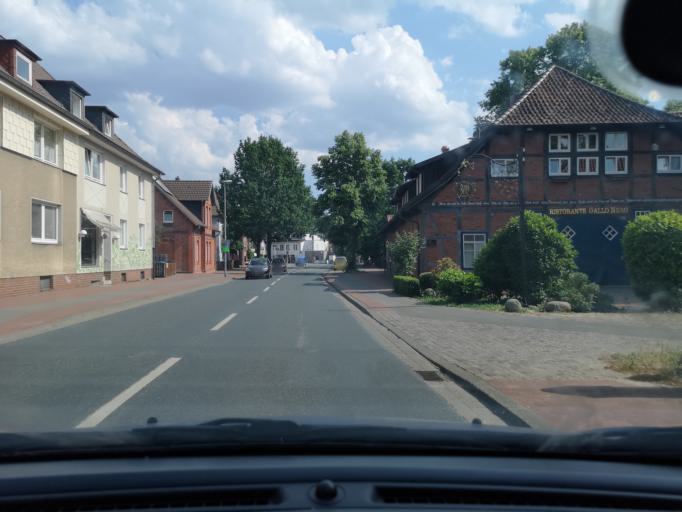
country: DE
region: Lower Saxony
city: Hannover
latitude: 52.4005
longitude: 9.8040
